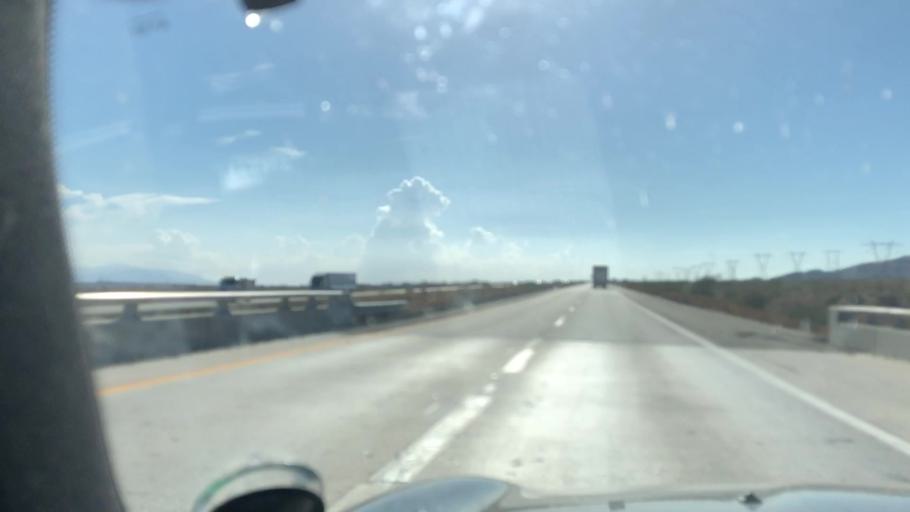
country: US
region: California
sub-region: Riverside County
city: Mecca
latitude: 33.6727
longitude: -115.9300
